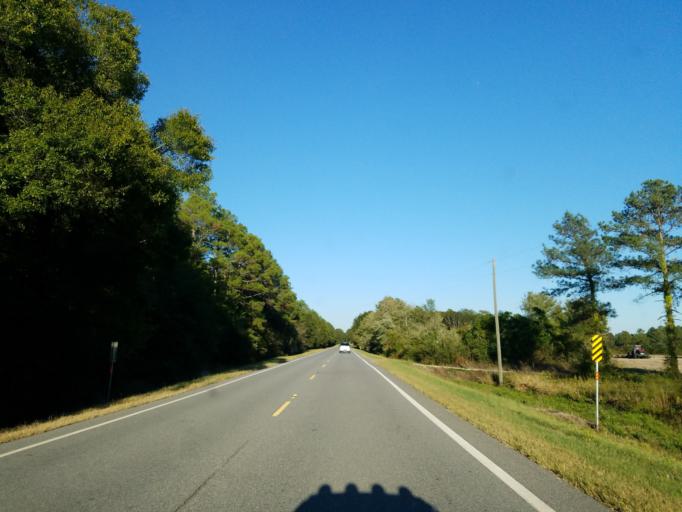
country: US
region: Georgia
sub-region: Lee County
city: Leesburg
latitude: 31.7302
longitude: -83.9561
